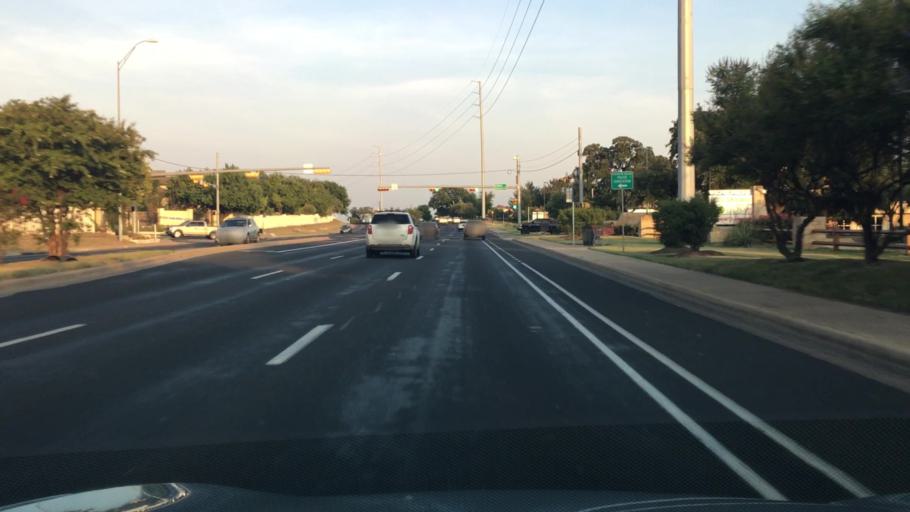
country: US
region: Texas
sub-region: Travis County
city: Onion Creek
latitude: 30.1697
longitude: -97.7965
